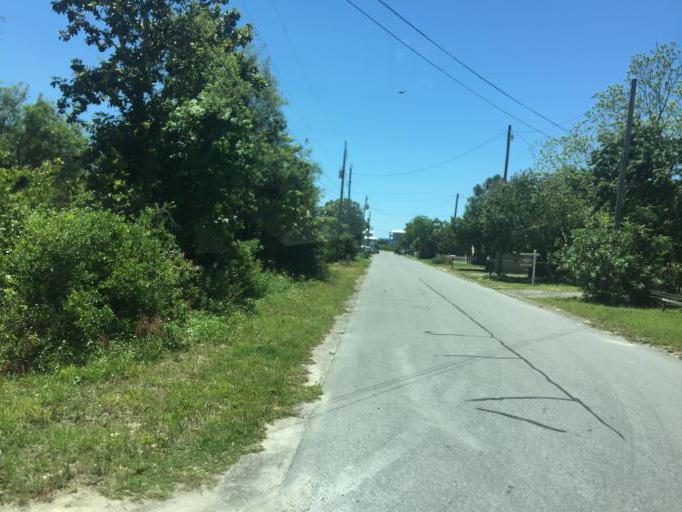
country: US
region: Florida
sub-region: Bay County
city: Laguna Beach
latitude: 30.2463
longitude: -85.9293
